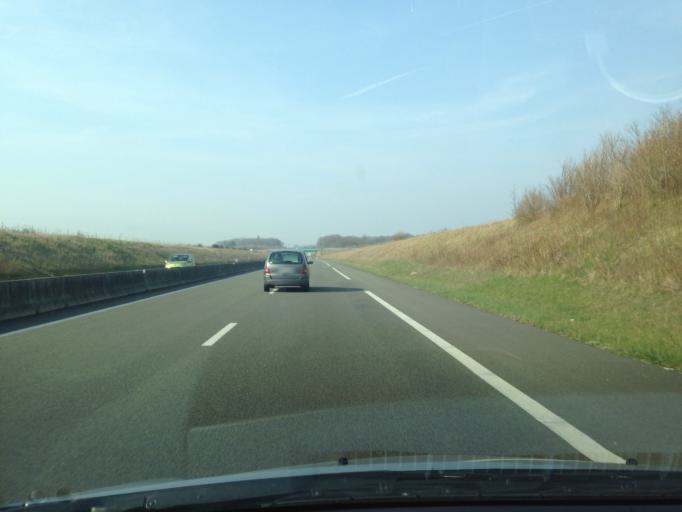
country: FR
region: Picardie
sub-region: Departement de la Somme
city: Nouvion
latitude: 50.2318
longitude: 1.7520
